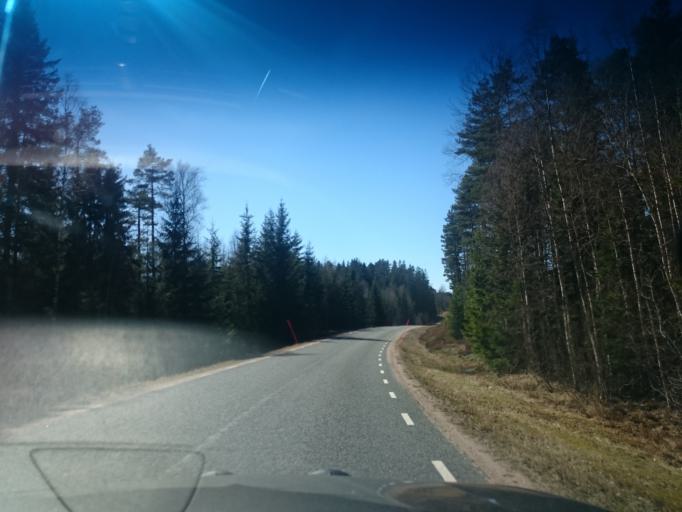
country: SE
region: Joenkoeping
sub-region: Vetlanda Kommun
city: Vetlanda
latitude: 57.2518
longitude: 15.0629
